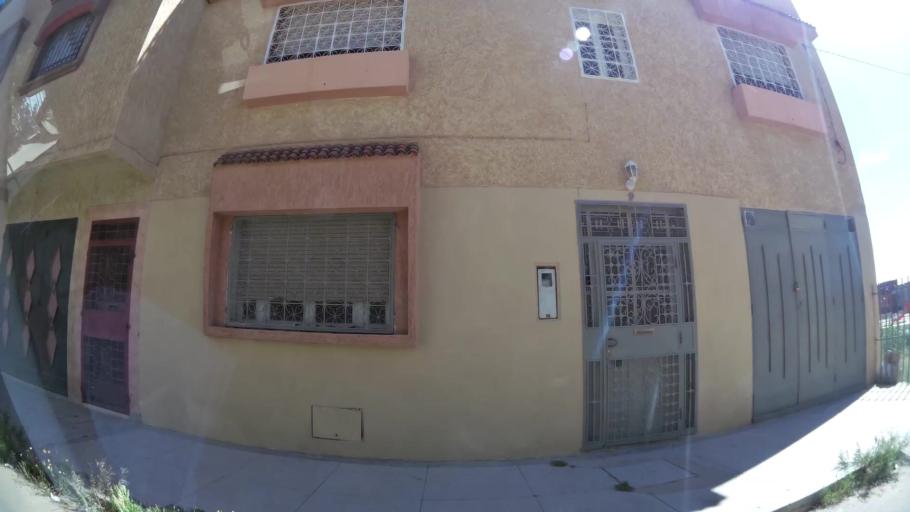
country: MA
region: Oriental
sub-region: Oujda-Angad
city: Oujda
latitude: 34.6633
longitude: -1.9285
